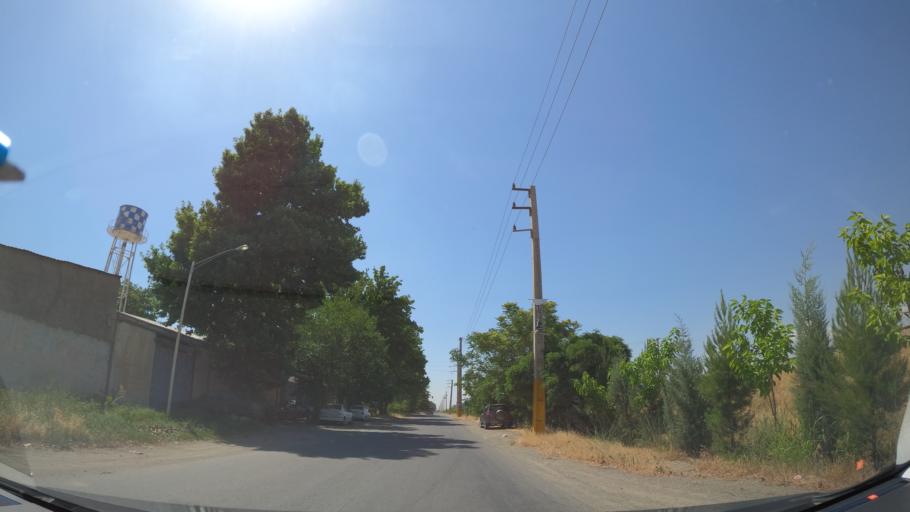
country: IR
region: Alborz
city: Hashtgerd
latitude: 35.9165
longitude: 50.7313
